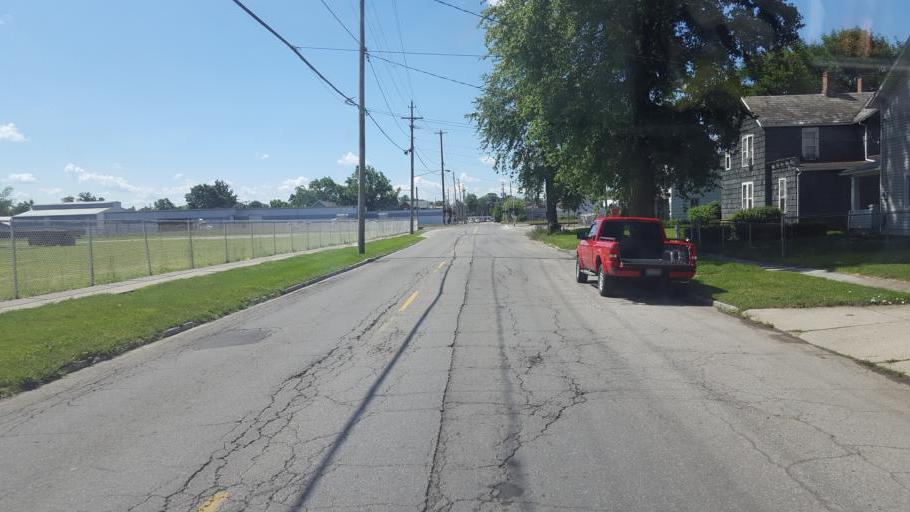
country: US
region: Ohio
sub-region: Marion County
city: Marion
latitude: 40.5920
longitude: -83.1205
